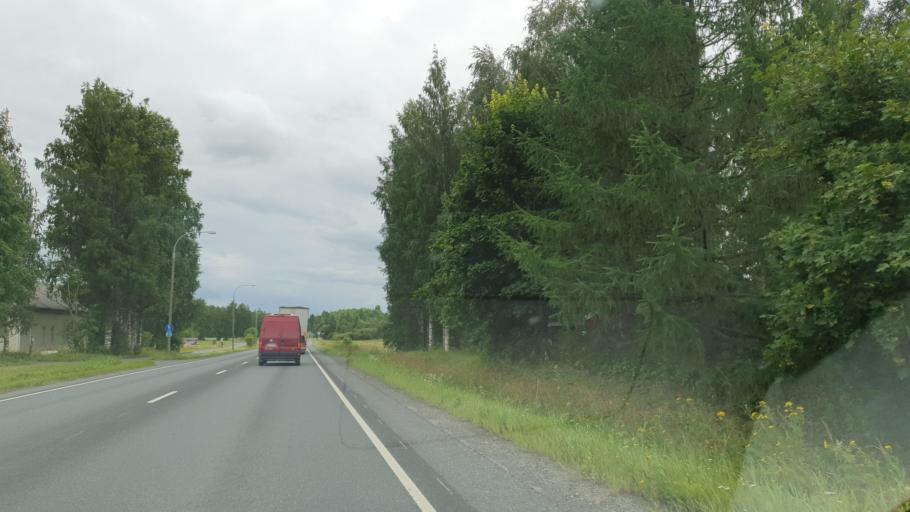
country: FI
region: Northern Savo
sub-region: Ylae-Savo
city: Lapinlahti
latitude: 63.4625
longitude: 27.3109
